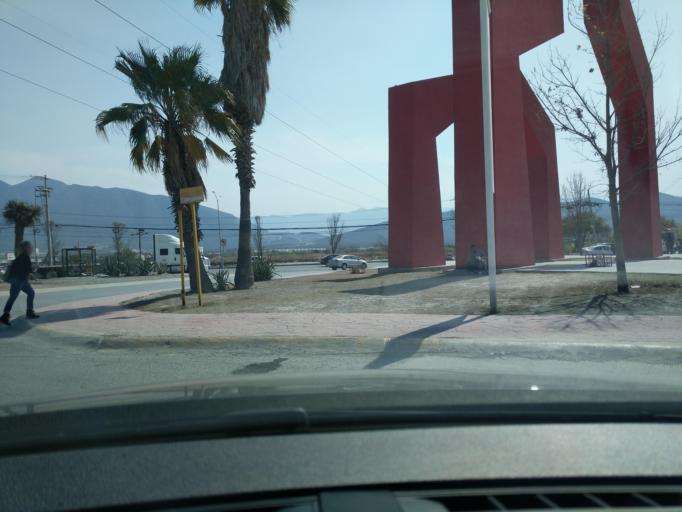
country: MX
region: Nuevo Leon
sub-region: Garcia
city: Valle de Lincoln
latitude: 25.7891
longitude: -100.4918
